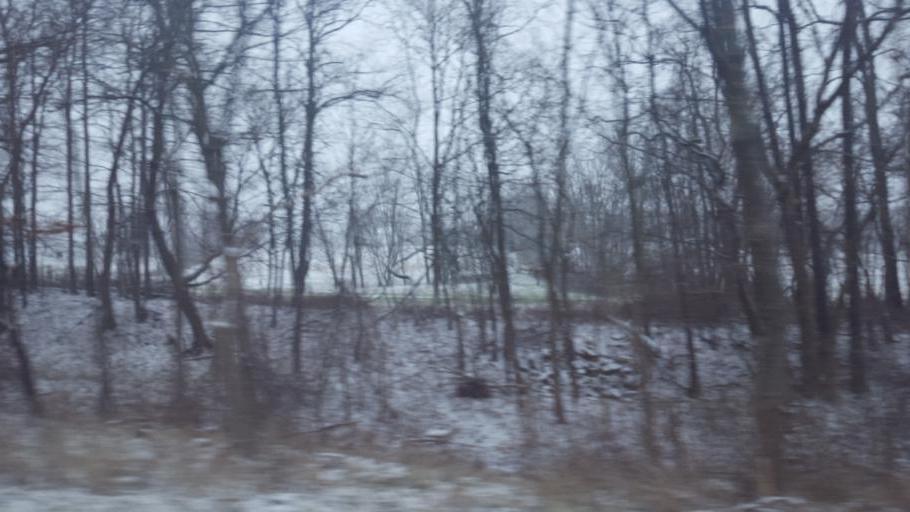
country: US
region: Ohio
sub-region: Coshocton County
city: West Lafayette
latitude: 40.3324
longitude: -81.7809
